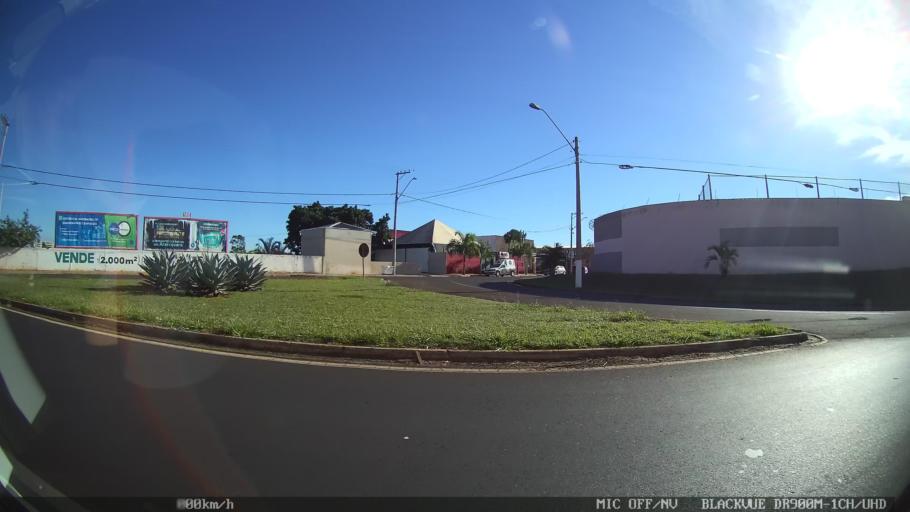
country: BR
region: Sao Paulo
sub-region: Araraquara
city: Araraquara
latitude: -21.7494
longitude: -48.1834
